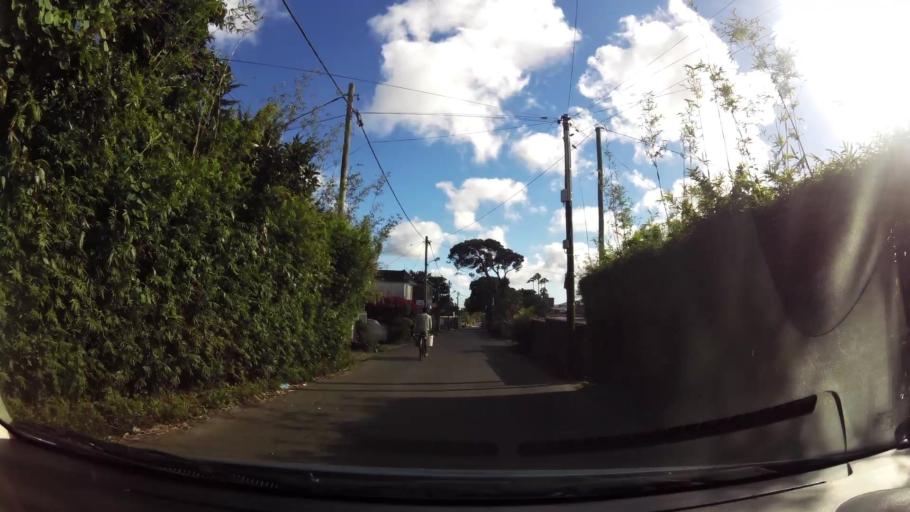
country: MU
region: Plaines Wilhems
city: Curepipe
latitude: -20.3048
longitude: 57.5169
